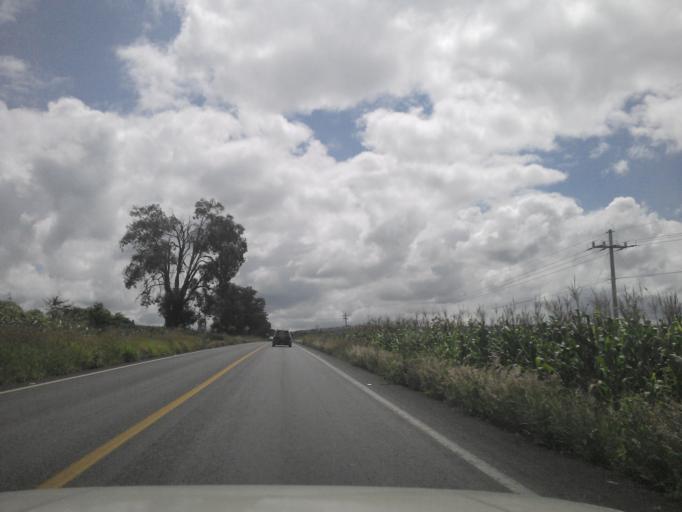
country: MX
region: Jalisco
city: Zapotlanejo
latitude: 20.6147
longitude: -102.9997
